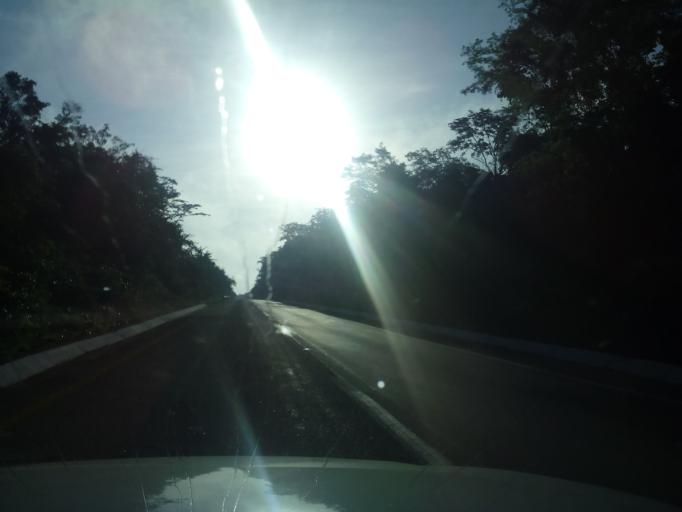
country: MX
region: Yucatan
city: Tunkas
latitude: 20.7631
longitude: -88.7900
